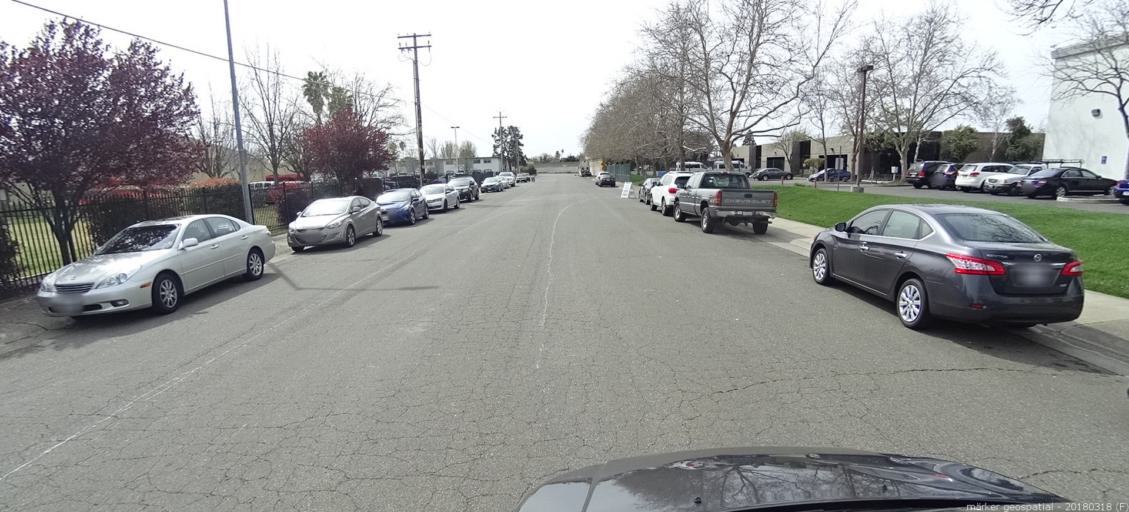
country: US
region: California
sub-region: Sacramento County
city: Parkway
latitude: 38.5072
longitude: -121.4553
